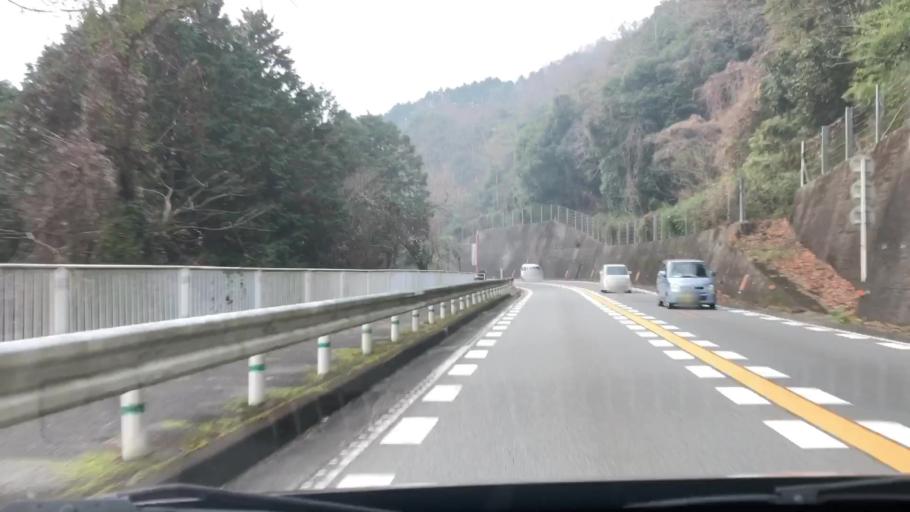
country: JP
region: Oita
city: Usuki
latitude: 33.0254
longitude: 131.6944
